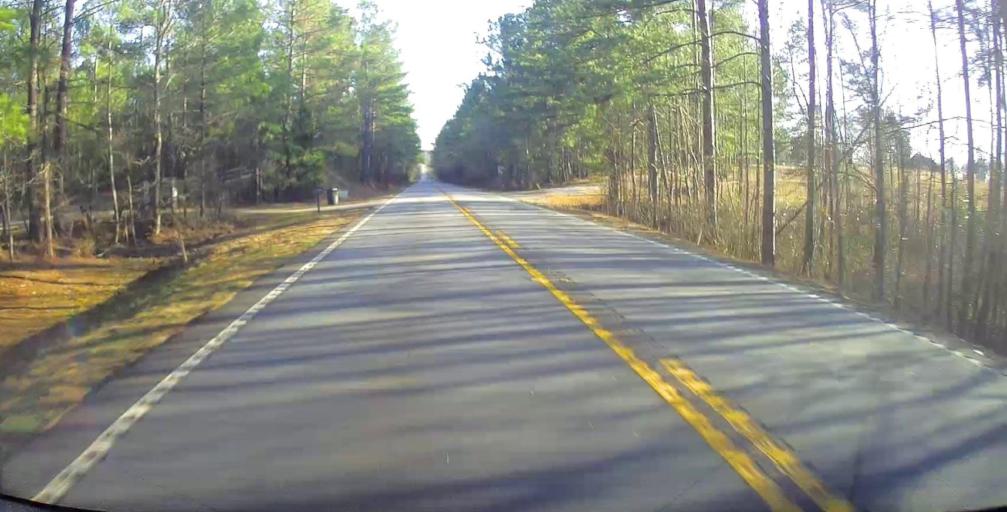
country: US
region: Alabama
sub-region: Chambers County
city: Valley
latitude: 32.8042
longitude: -85.1030
